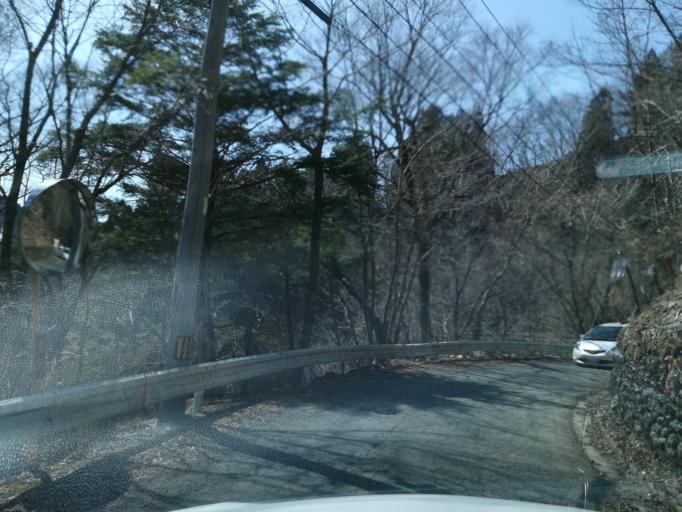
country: JP
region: Tokushima
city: Wakimachi
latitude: 33.8577
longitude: 134.0535
